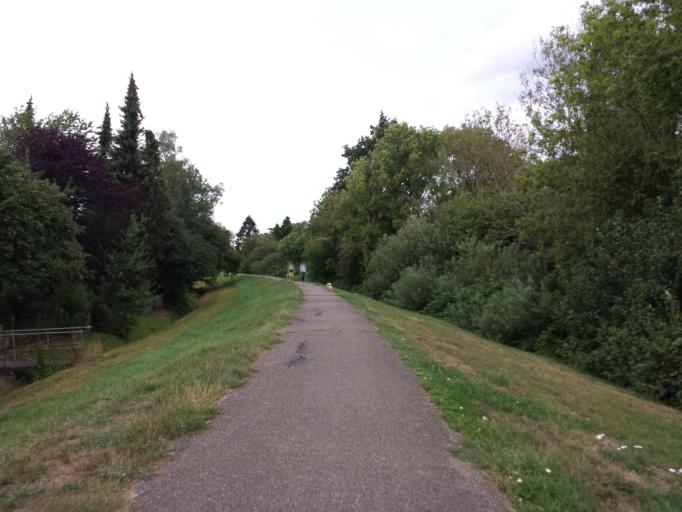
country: DE
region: Lower Saxony
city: Stuhr
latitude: 53.0619
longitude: 8.7682
